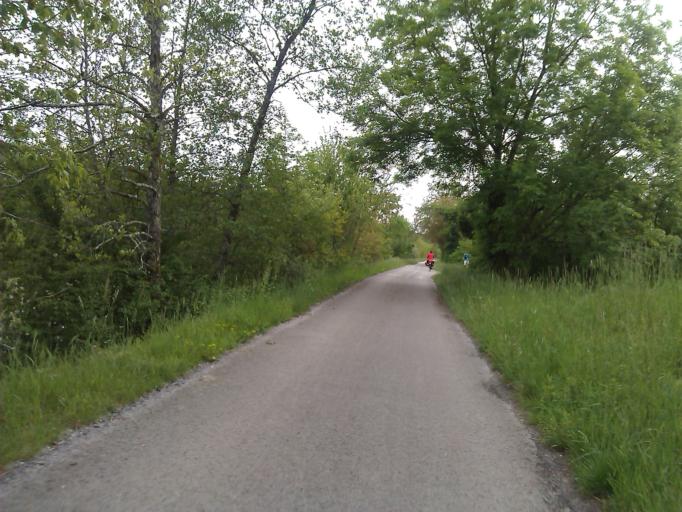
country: FR
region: Franche-Comte
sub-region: Departement du Jura
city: Fraisans
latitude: 47.1683
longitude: 5.7828
